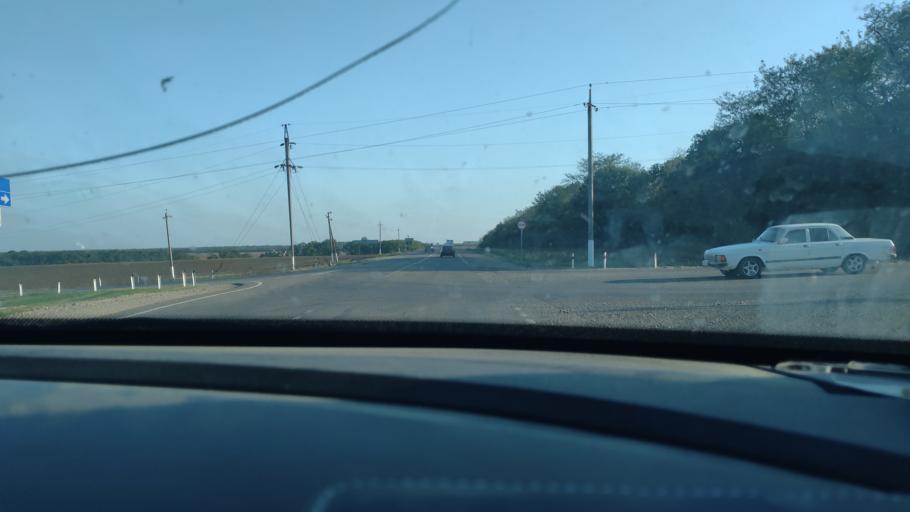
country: RU
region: Krasnodarskiy
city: Novominskaya
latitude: 46.2988
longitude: 38.9329
